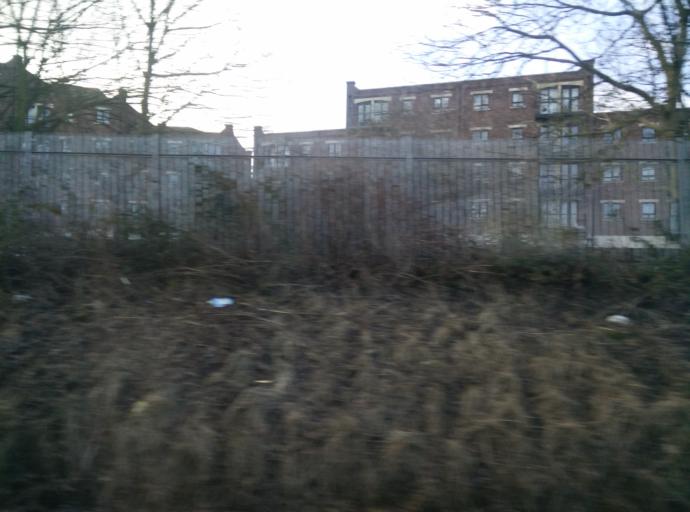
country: GB
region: Northern Ireland
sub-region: City of Belfast
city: Belfast
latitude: 54.5879
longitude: -5.9284
